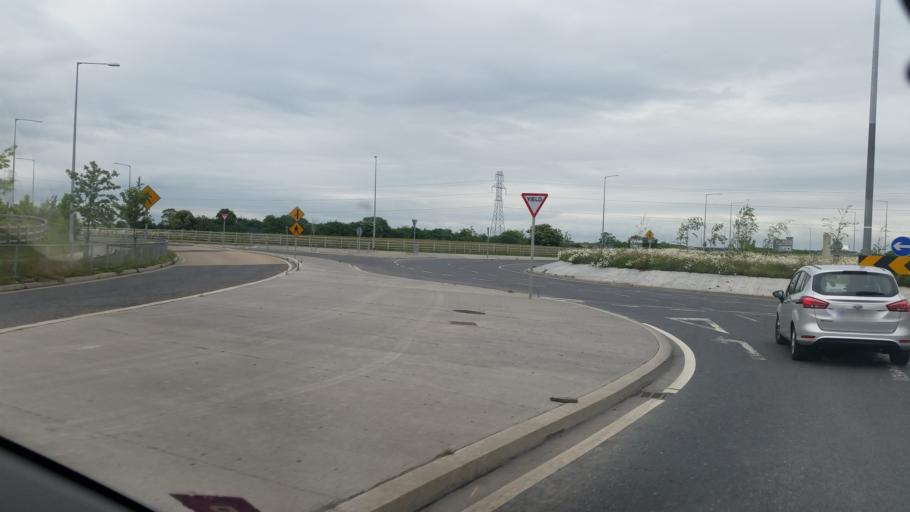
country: IE
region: Leinster
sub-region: Fingal County
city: Blanchardstown
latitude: 53.4287
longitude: -6.3531
